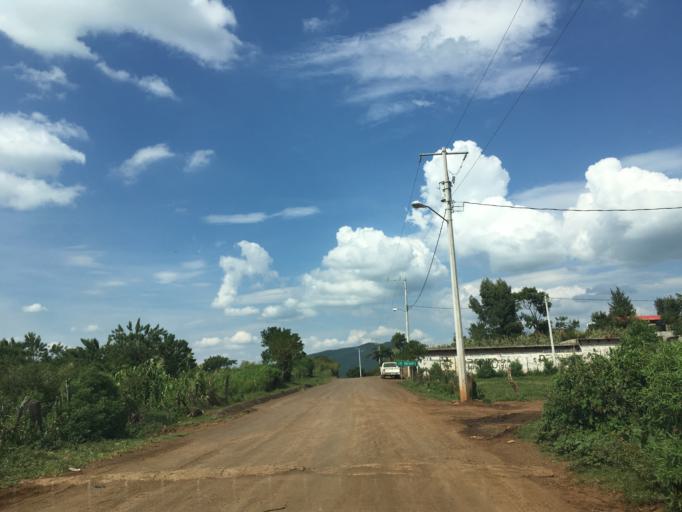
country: MX
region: Mexico
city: El Guayabito
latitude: 19.8940
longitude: -102.4956
